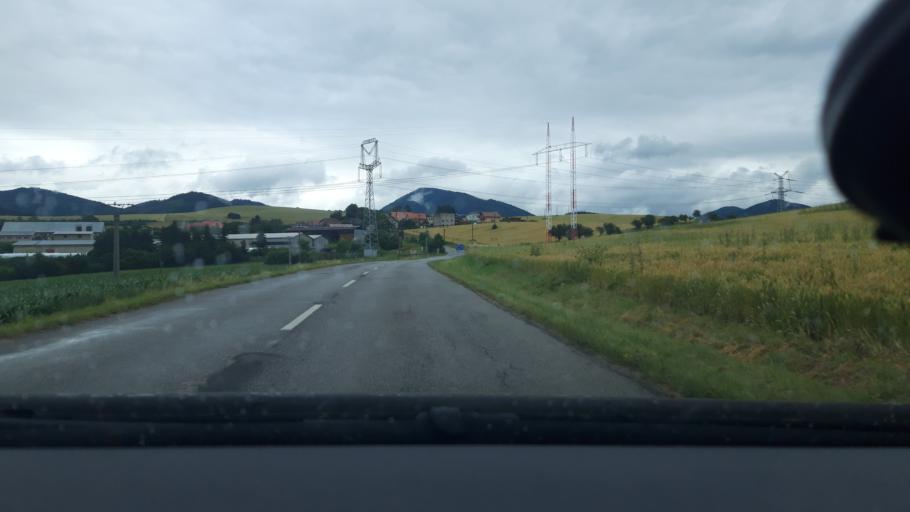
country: SK
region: Zilinsky
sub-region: Okres Martin
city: Martin
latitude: 49.0391
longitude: 18.9773
